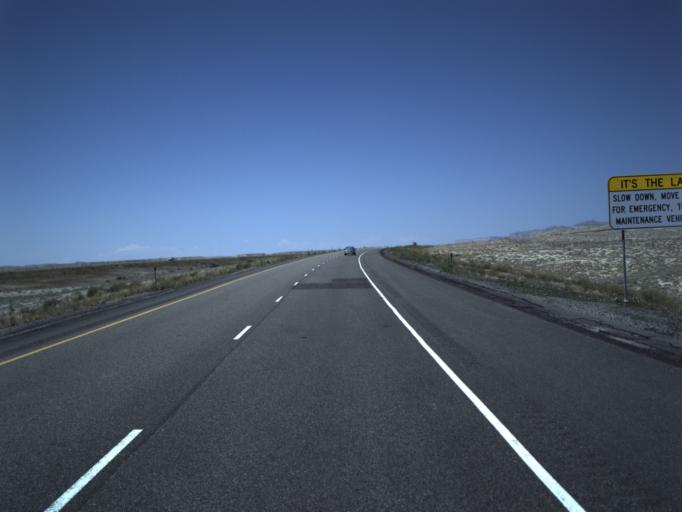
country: US
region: Utah
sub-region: Grand County
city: Moab
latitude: 38.9331
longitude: -109.4319
